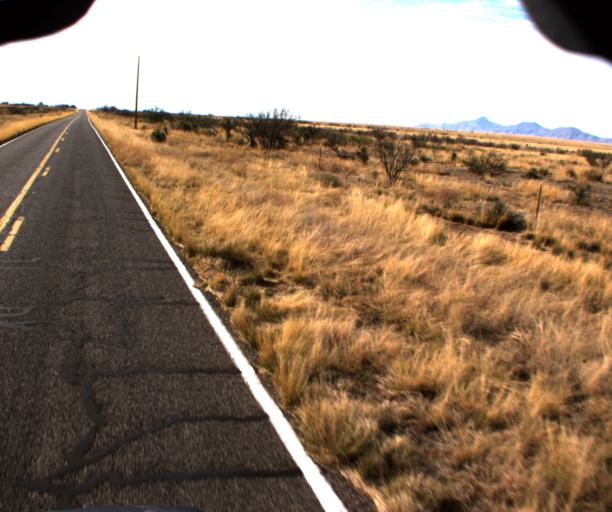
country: US
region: Arizona
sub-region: Cochise County
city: Willcox
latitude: 32.0228
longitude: -109.4422
